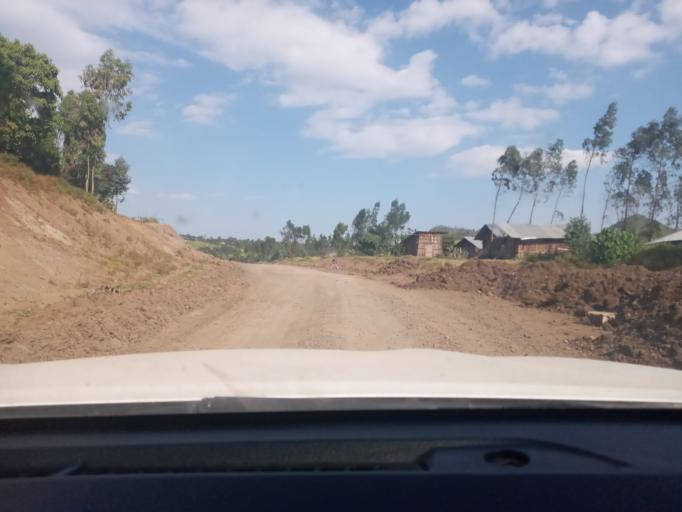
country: ET
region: Amhara
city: Were Ilu
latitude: 10.6142
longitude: 39.0421
